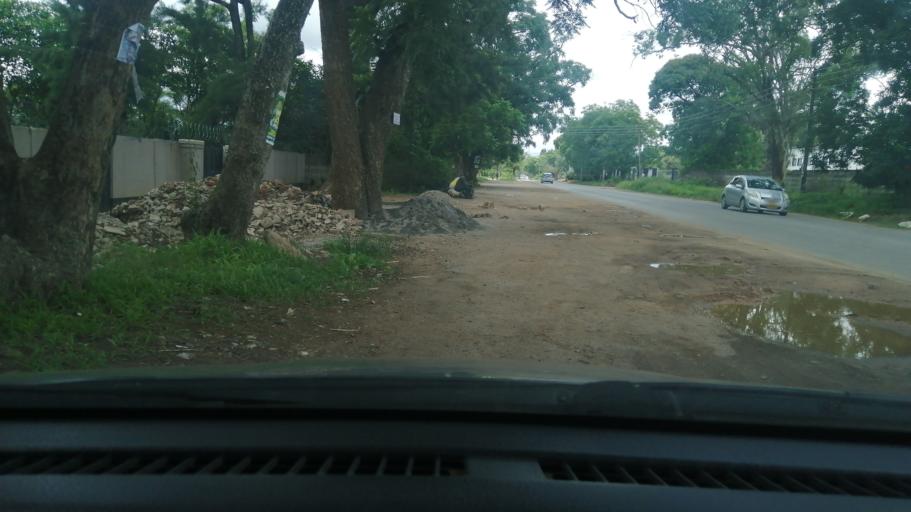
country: ZW
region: Harare
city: Harare
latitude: -17.8846
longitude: 31.0734
